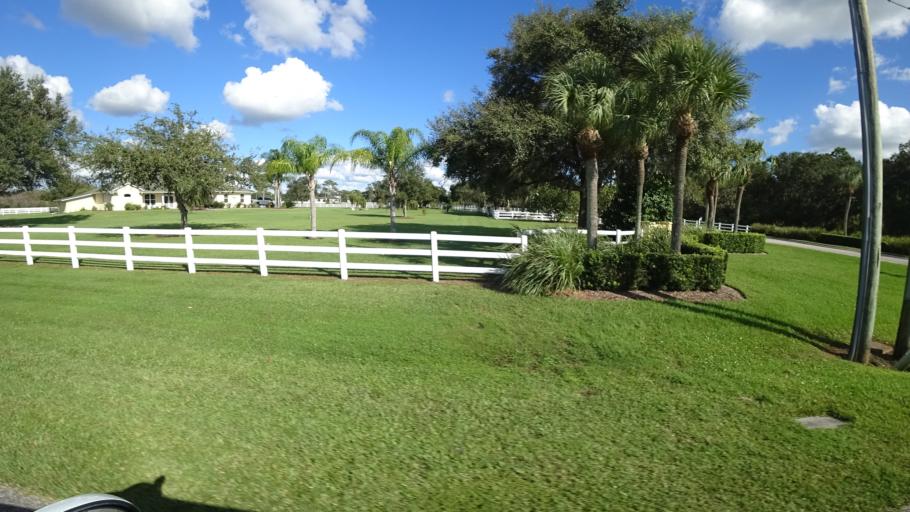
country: US
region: Florida
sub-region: Sarasota County
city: Lake Sarasota
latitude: 27.3437
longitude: -82.2692
